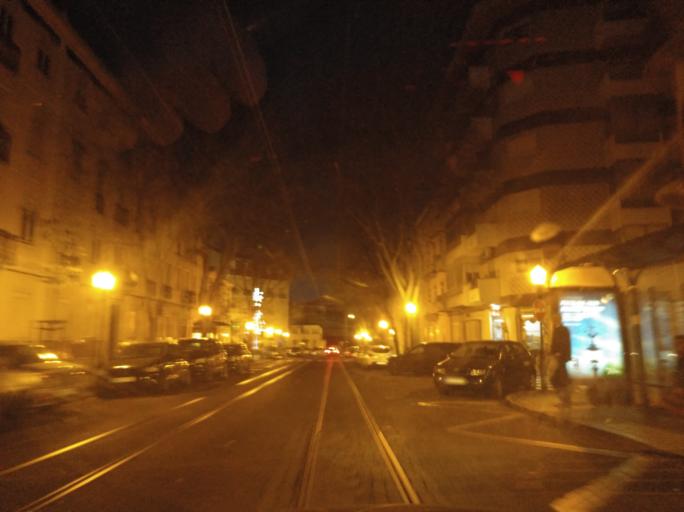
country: PT
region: Setubal
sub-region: Almada
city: Pragal
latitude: 38.7052
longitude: -9.1856
